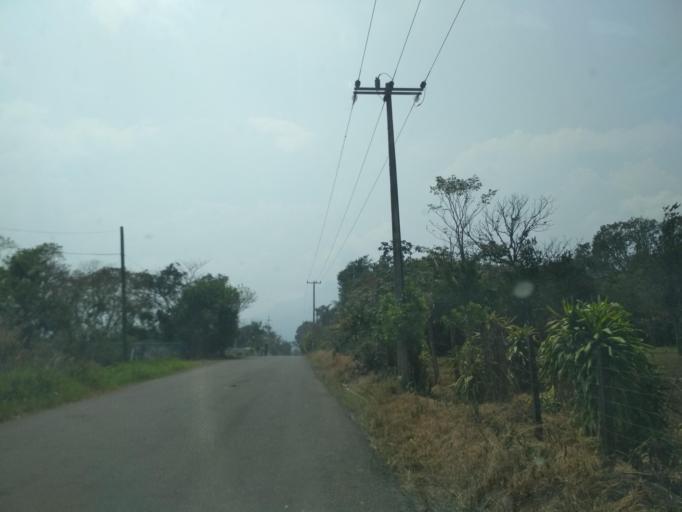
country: MX
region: Veracruz
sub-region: Cordoba
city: Fredepo
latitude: 18.8608
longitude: -96.9838
